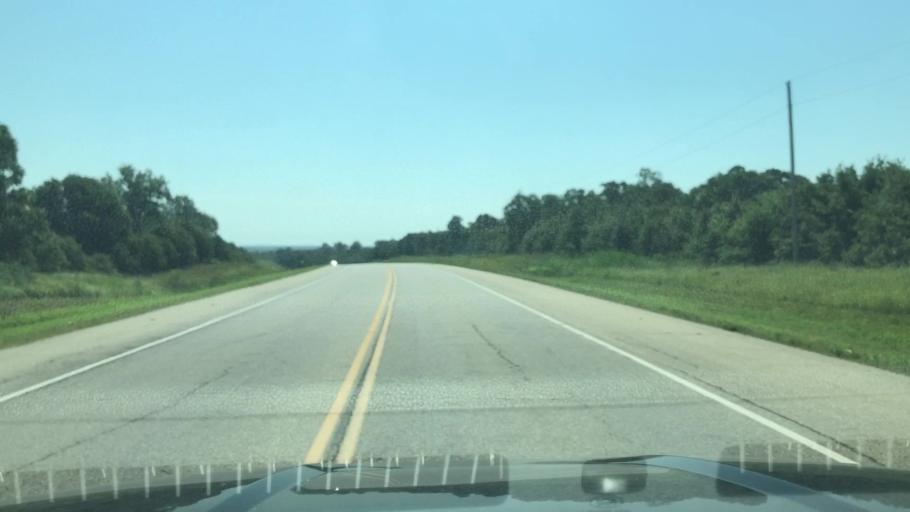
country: US
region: Oklahoma
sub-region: Creek County
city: Kellyville
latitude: 35.9895
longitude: -96.3478
